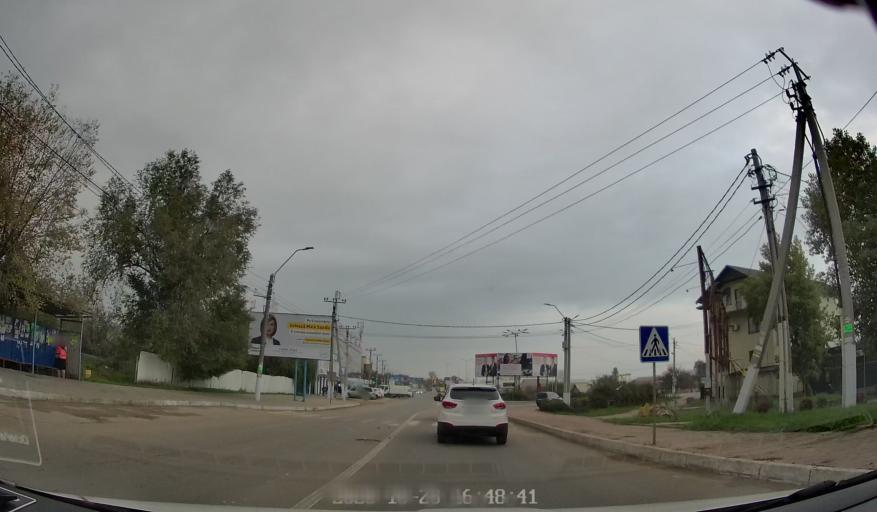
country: MD
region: Gagauzia
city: Comrat
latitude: 46.3059
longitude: 28.6574
